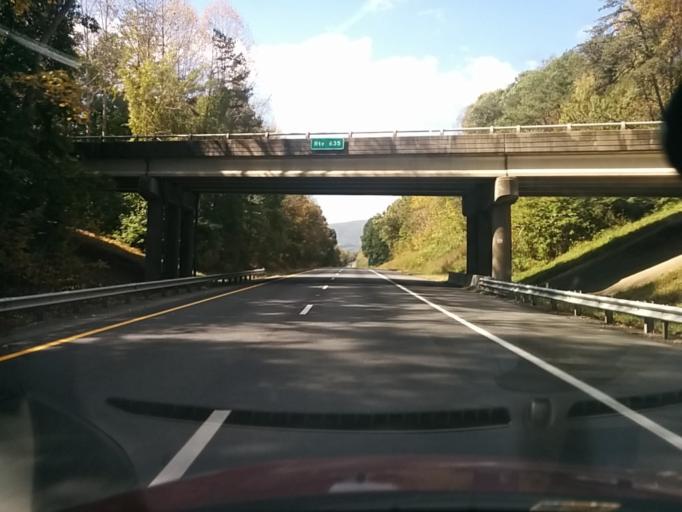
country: US
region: Virginia
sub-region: Albemarle County
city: Crozet
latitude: 38.0370
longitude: -78.7009
